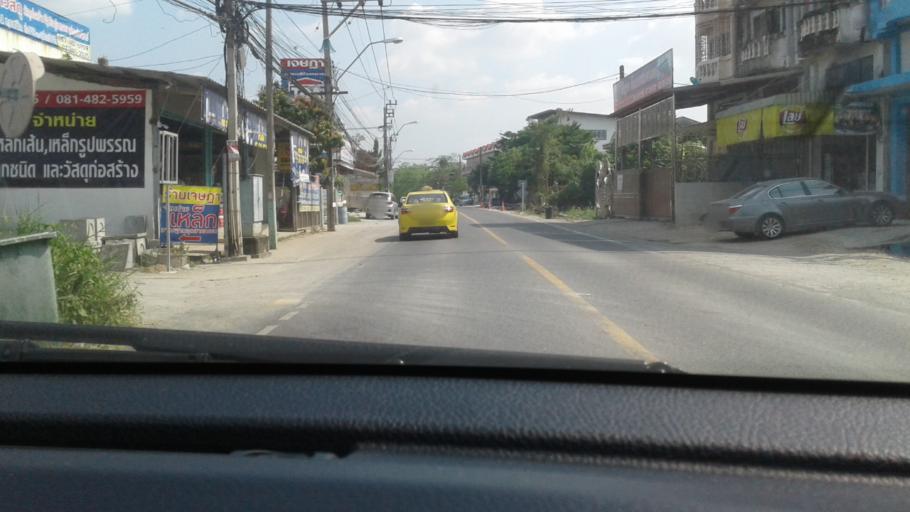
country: TH
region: Nonthaburi
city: Bang Yai
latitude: 13.7971
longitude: 100.3851
